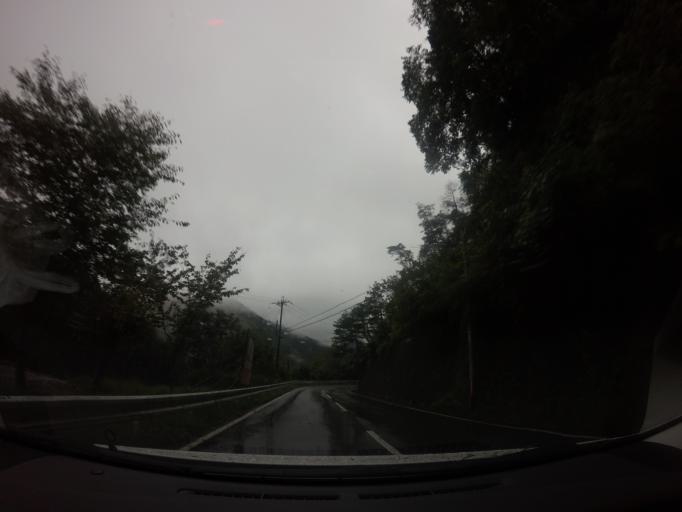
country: JP
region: Wakayama
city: Koya
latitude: 34.0630
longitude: 135.7519
